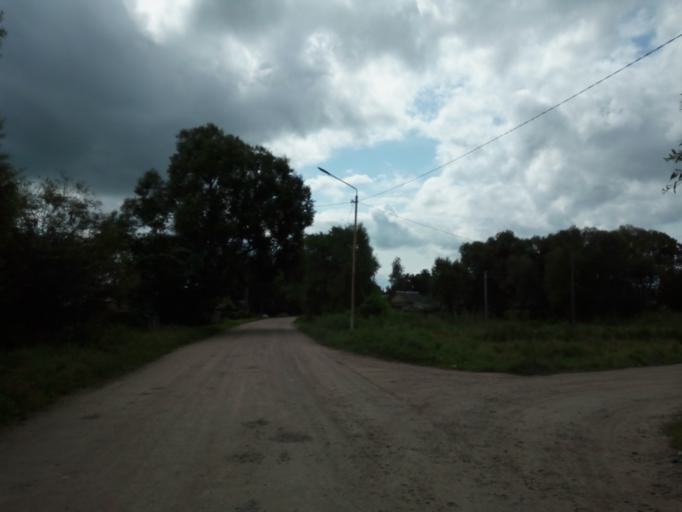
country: RU
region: Primorskiy
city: Dal'nerechensk
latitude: 45.9348
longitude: 133.8149
